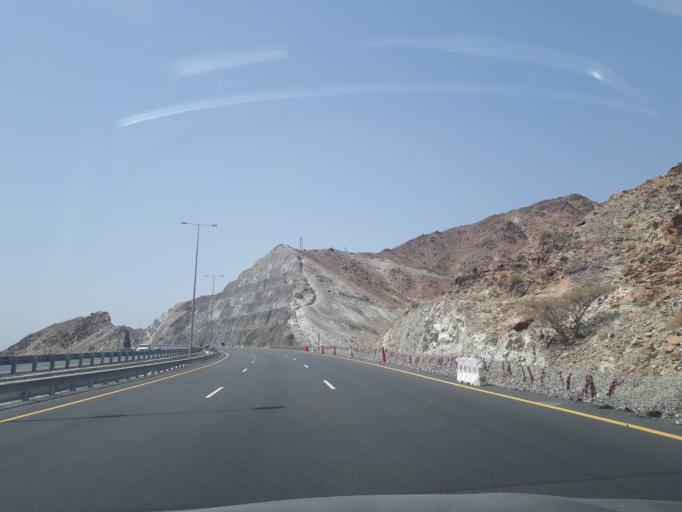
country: OM
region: Muhafazat ad Dakhiliyah
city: Bidbid
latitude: 23.3744
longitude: 58.1024
